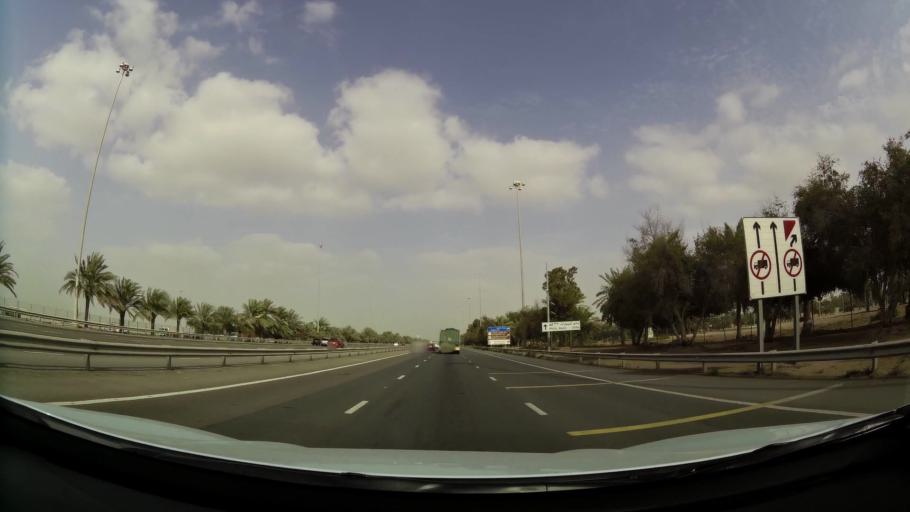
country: AE
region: Abu Dhabi
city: Abu Dhabi
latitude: 24.4227
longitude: 54.5225
